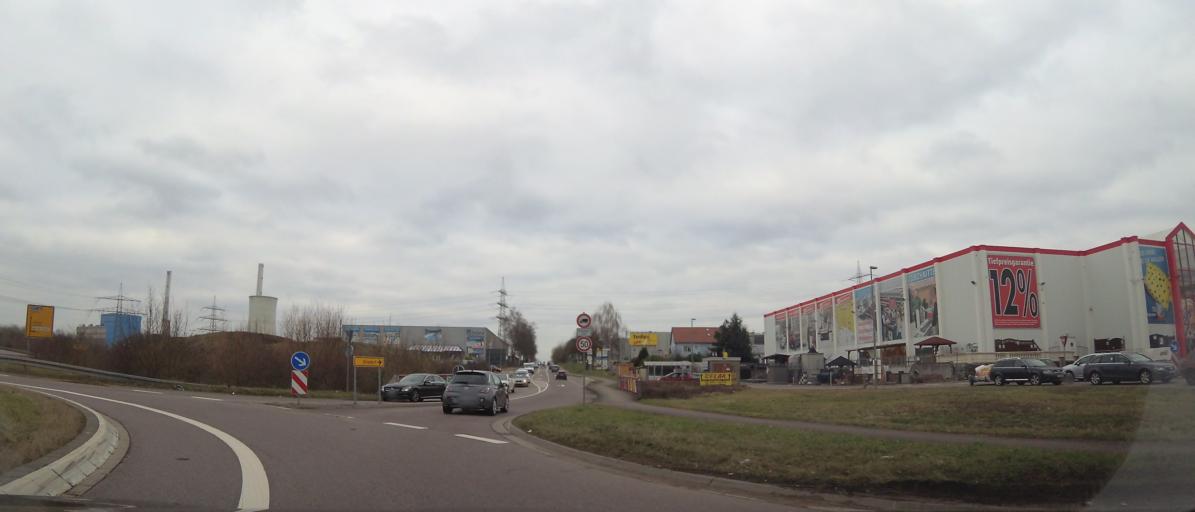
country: DE
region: Saarland
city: Ensdorf
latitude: 49.2893
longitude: 6.7827
